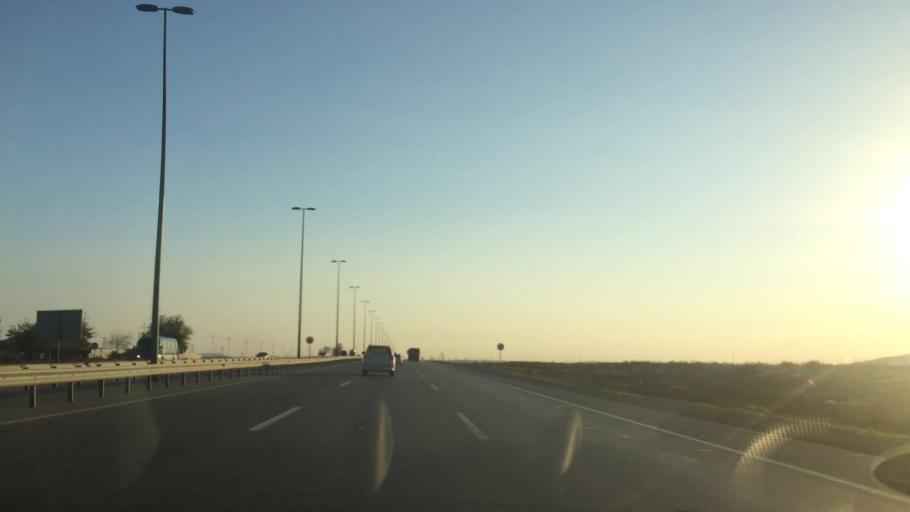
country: AZ
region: Baki
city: Qobustan
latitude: 39.9895
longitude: 49.4292
